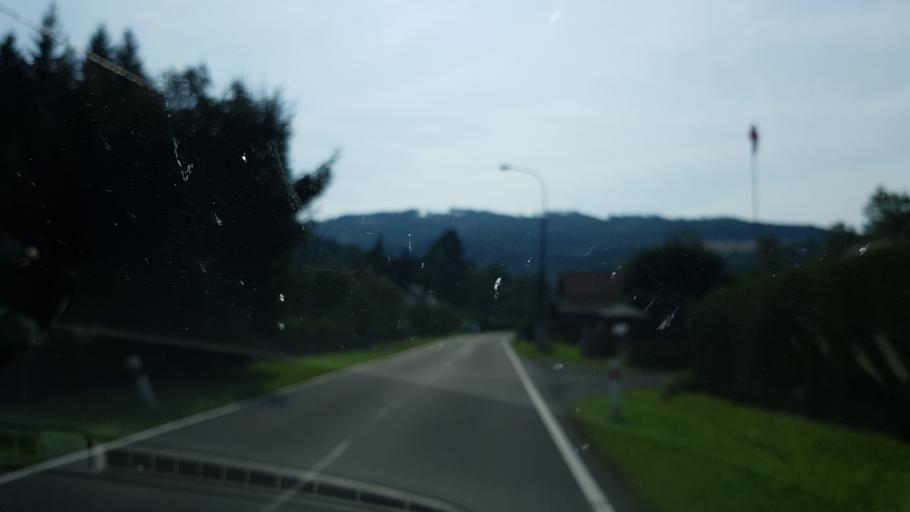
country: CZ
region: Olomoucky
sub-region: Okres Jesenik
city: Jesenik
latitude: 50.2103
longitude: 17.2280
